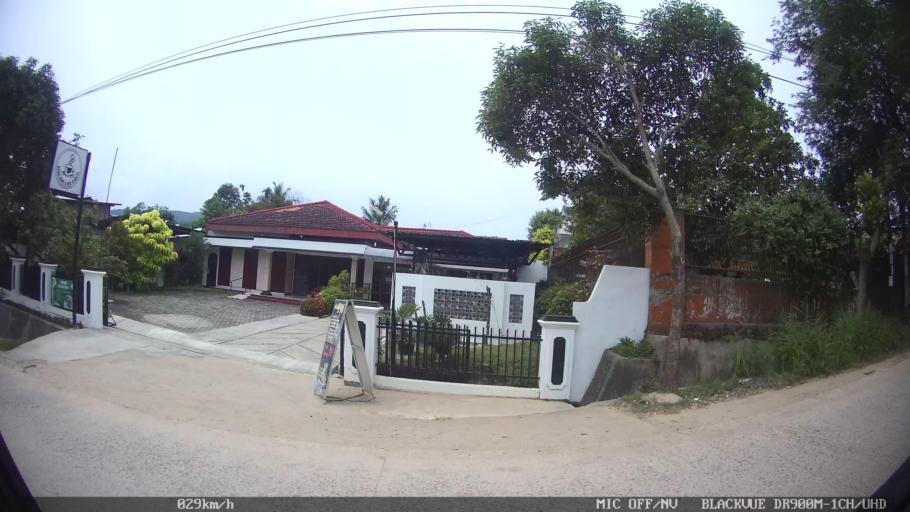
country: ID
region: Lampung
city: Bandarlampung
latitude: -5.4070
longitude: 105.2984
